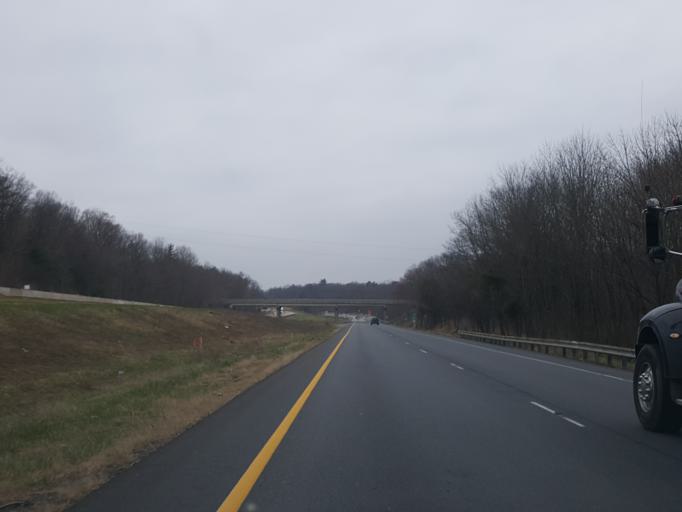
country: US
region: Pennsylvania
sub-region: Lebanon County
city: Fredericksburg
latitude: 40.5180
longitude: -76.4698
